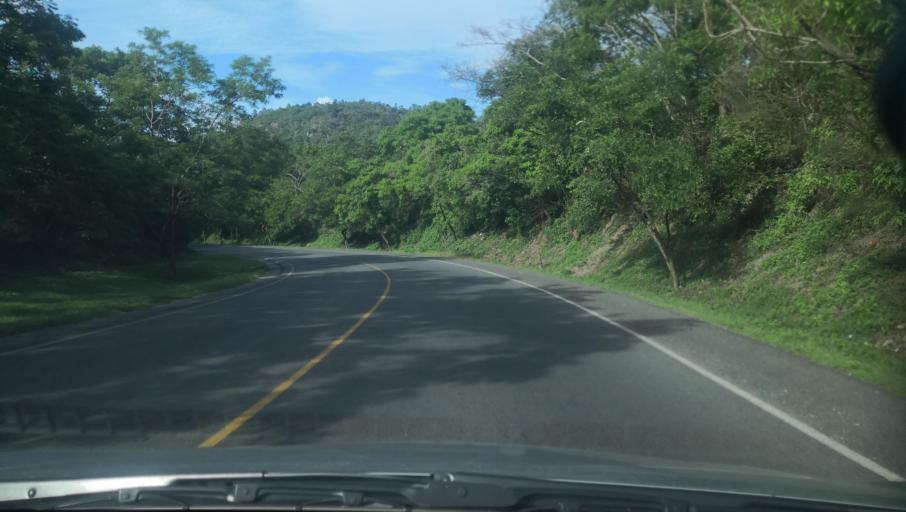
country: NI
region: Madriz
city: Totogalpa
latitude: 13.5768
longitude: -86.4774
